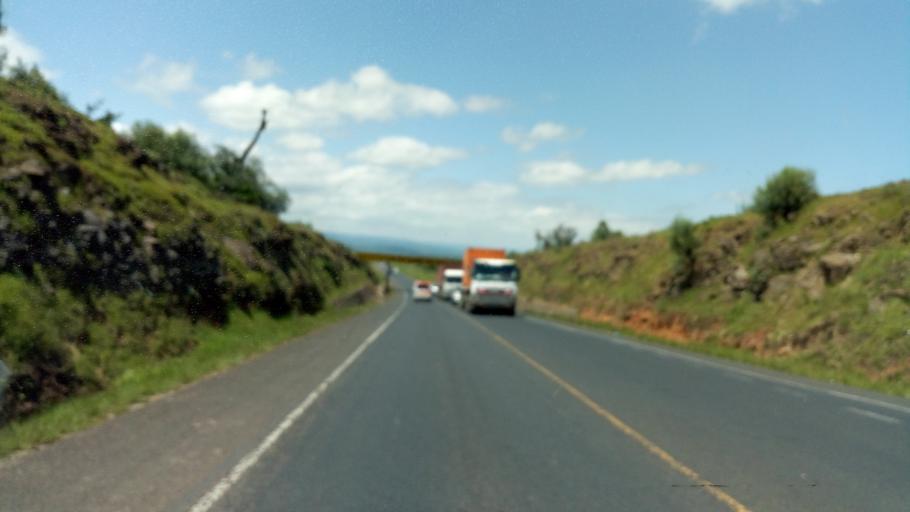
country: KE
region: Nakuru
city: Naivasha
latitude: -0.5427
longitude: 36.3395
